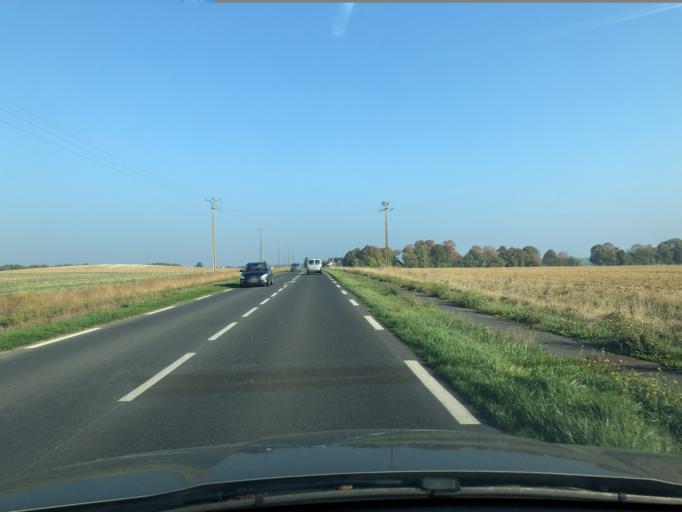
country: FR
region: Centre
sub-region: Departement d'Indre-et-Loire
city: Chanceaux-sur-Choisille
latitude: 47.4843
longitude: 0.6971
